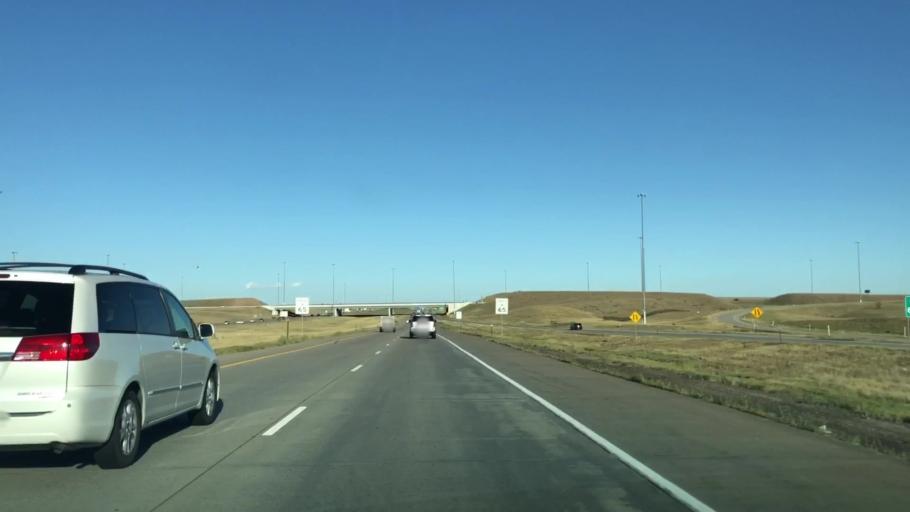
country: US
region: Colorado
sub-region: Adams County
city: Aurora
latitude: 39.8340
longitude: -104.7550
